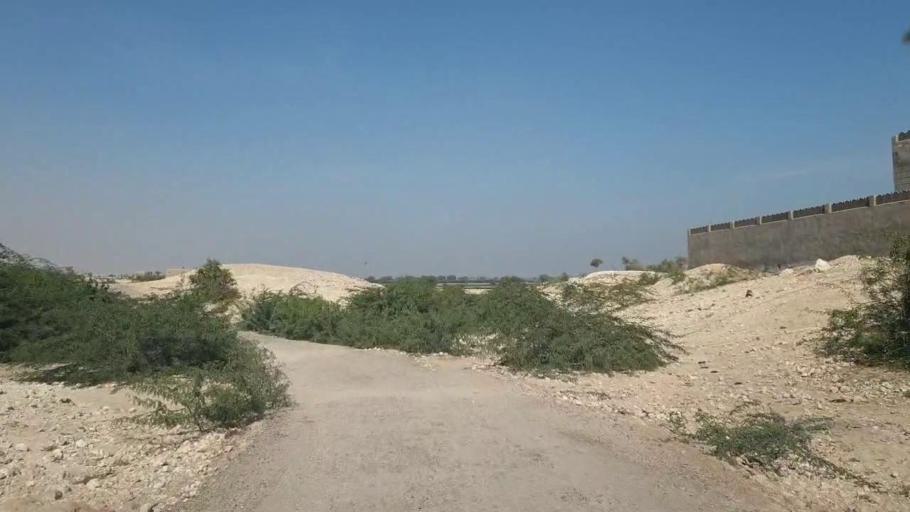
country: PK
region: Sindh
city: Hala
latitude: 25.7343
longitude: 68.2962
